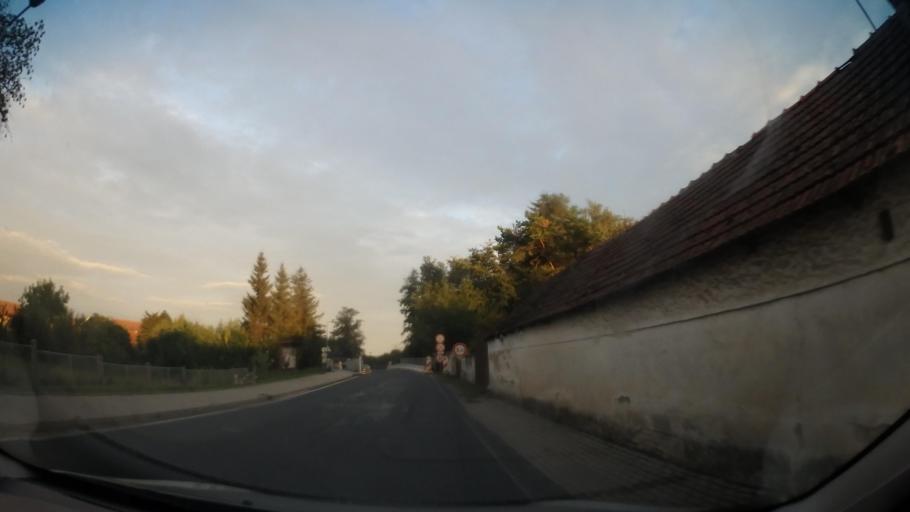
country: CZ
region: Central Bohemia
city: Milovice
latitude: 50.2265
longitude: 14.9380
